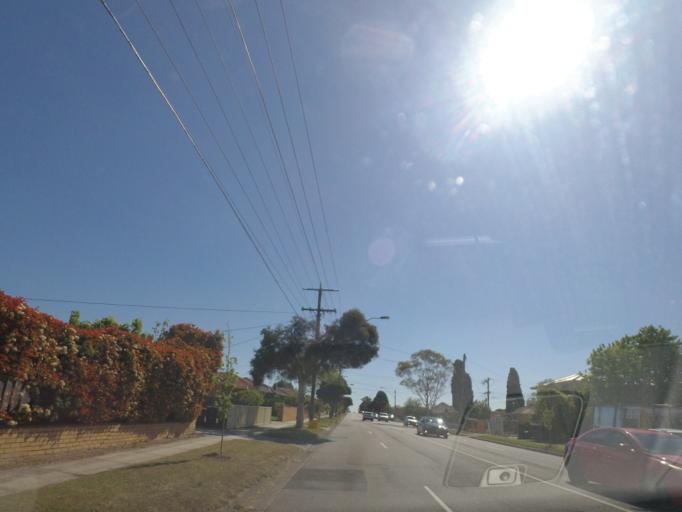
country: AU
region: Victoria
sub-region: Greater Dandenong
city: Noble Park
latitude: -37.9638
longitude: 145.1635
